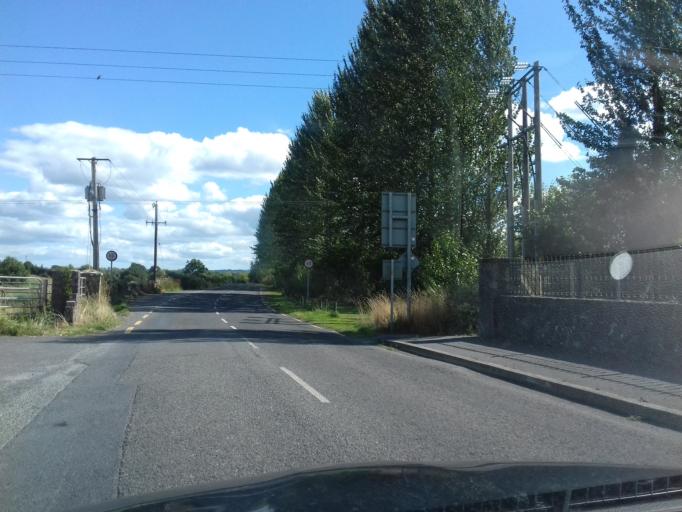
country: IE
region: Leinster
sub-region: Kilkenny
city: Callan
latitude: 52.5416
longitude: -7.3823
